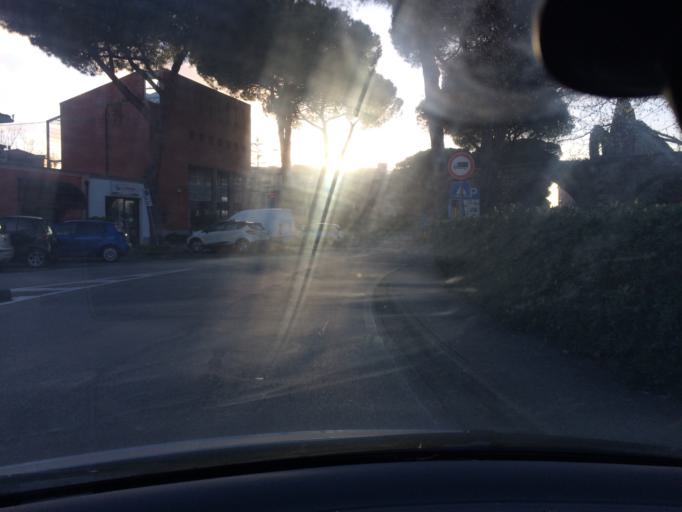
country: IT
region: Tuscany
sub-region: Province of Pisa
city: Pisa
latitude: 43.7209
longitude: 10.4219
